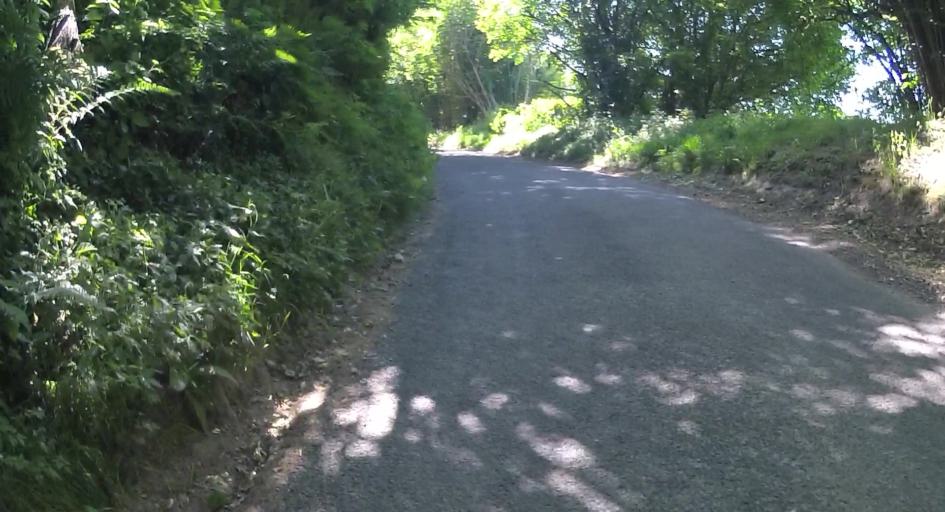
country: GB
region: England
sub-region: Hampshire
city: Kingsclere
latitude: 51.3267
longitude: -1.2908
